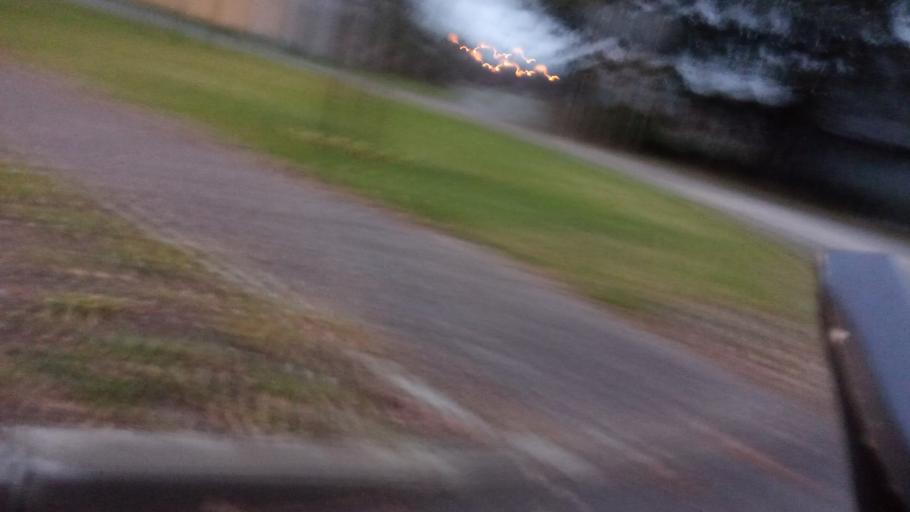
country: EE
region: Harju
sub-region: Kuusalu vald
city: Kuusalu
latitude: 59.4460
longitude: 25.4488
